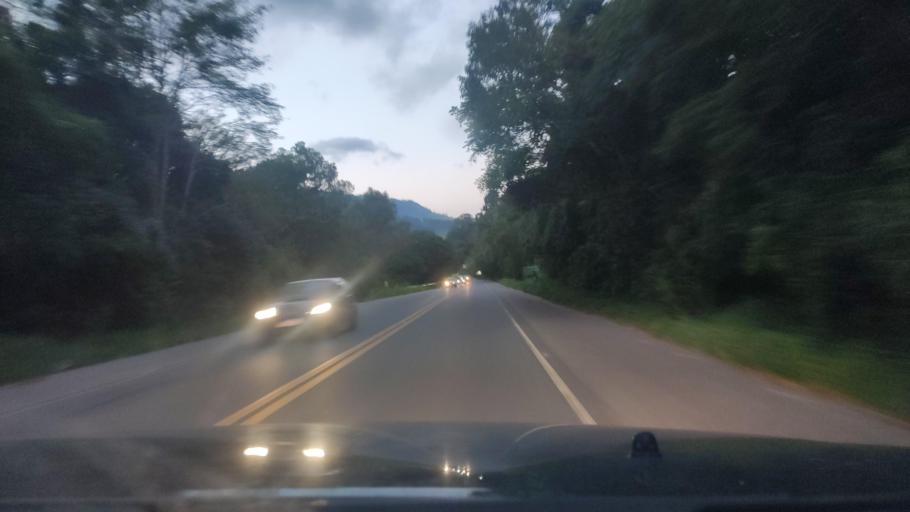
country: BR
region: Sao Paulo
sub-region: Campos Do Jordao
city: Campos do Jordao
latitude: -22.7602
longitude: -45.7413
